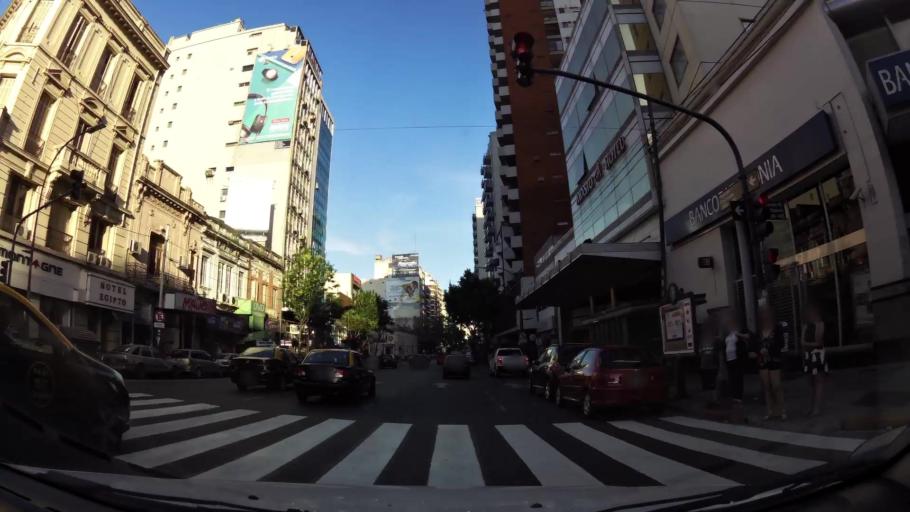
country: AR
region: Buenos Aires F.D.
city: Retiro
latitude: -34.6040
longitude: -58.4103
